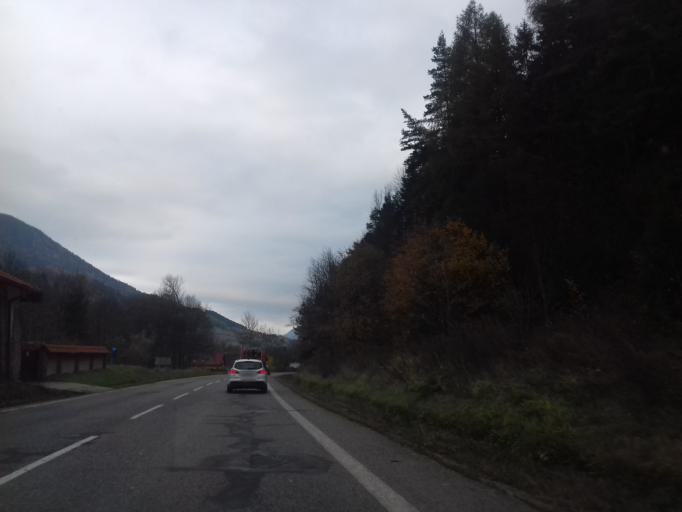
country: SK
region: Zilinsky
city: Ruzomberok
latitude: 49.0221
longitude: 19.2926
